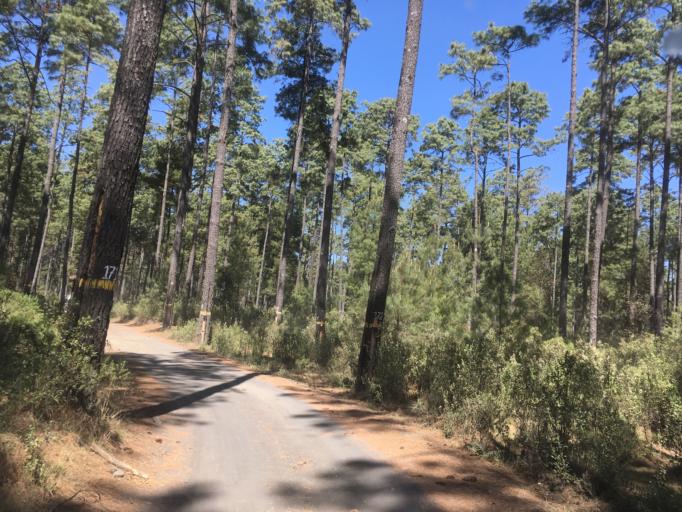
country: MX
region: Michoacan
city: Nuevo San Juan Parangaricutiro
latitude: 19.4602
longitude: -102.2092
